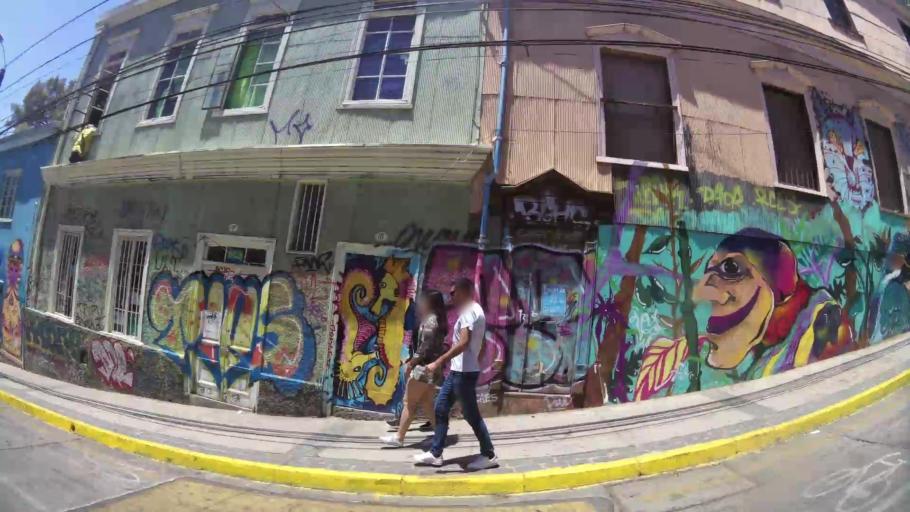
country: CL
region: Valparaiso
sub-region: Provincia de Valparaiso
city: Valparaiso
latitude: -33.0445
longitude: -71.6263
